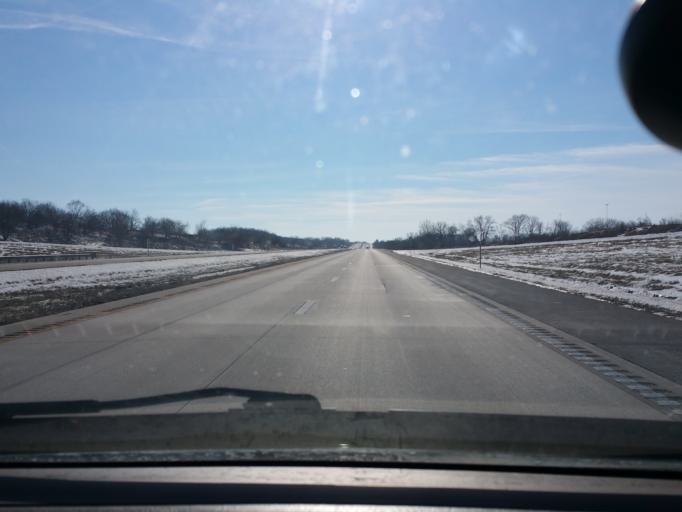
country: US
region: Missouri
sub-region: Daviess County
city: Gallatin
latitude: 39.9961
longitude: -94.0958
